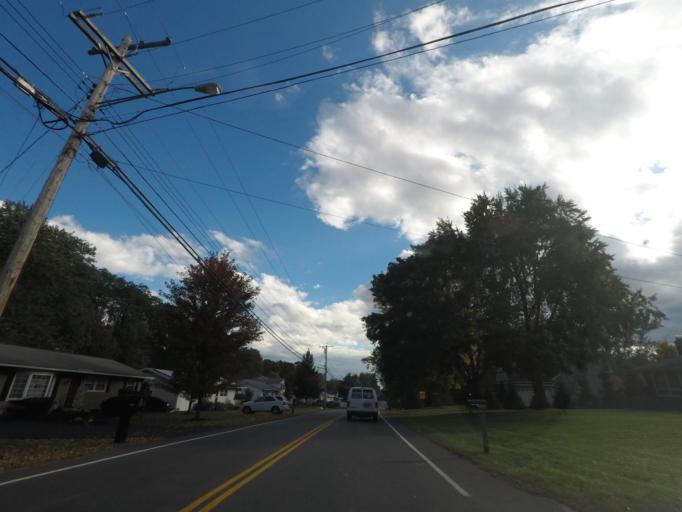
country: US
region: New York
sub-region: Schenectady County
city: Niskayuna
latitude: 42.7566
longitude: -73.8393
